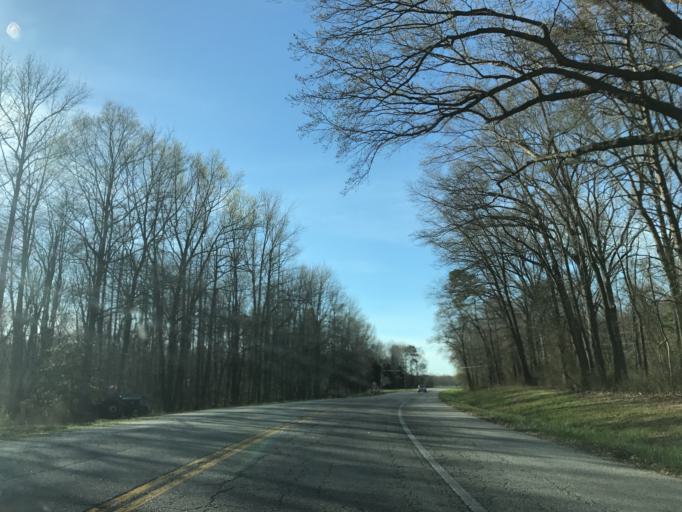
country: US
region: Maryland
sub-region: Caroline County
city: Greensboro
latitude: 39.1164
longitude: -75.7563
